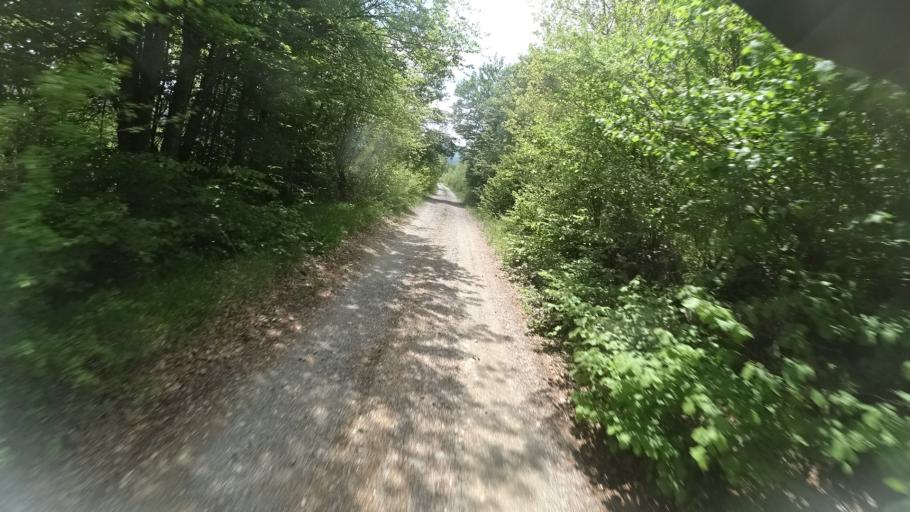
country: HR
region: Zadarska
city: Gracac
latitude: 44.5044
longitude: 15.8804
